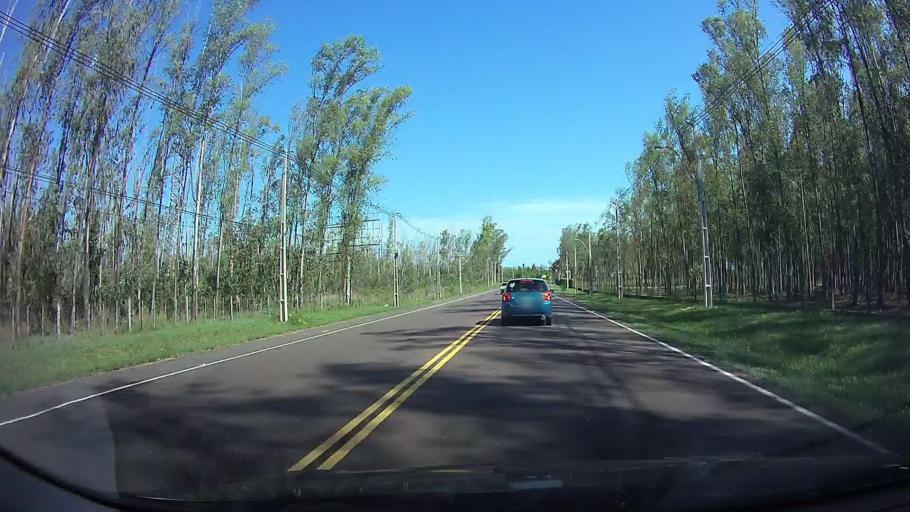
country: PY
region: Central
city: Ypacarai
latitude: -25.3788
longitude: -57.2627
